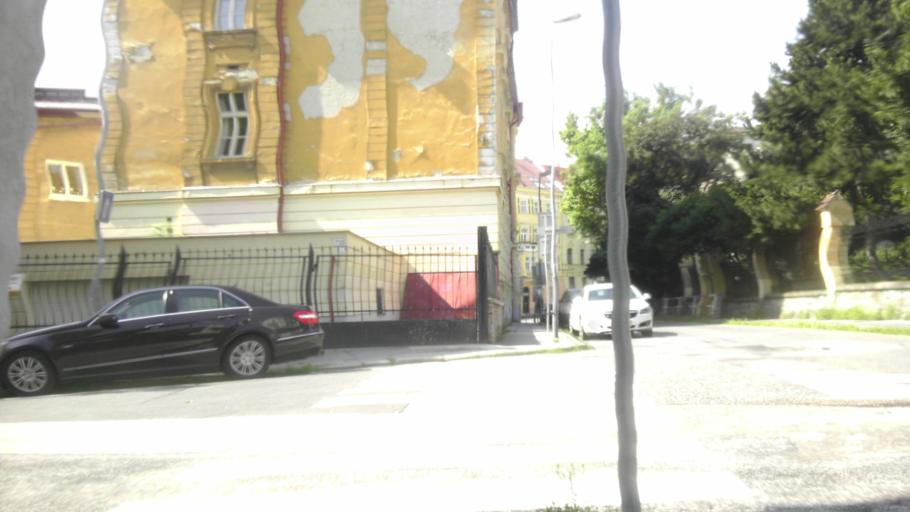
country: SK
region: Bratislavsky
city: Bratislava
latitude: 48.1498
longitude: 17.1040
